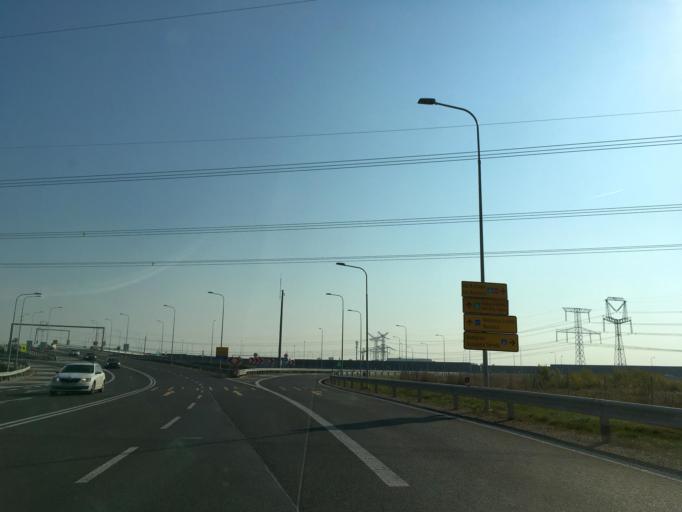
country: SK
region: Bratislavsky
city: Dunajska Luzna
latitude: 48.1118
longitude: 17.2210
